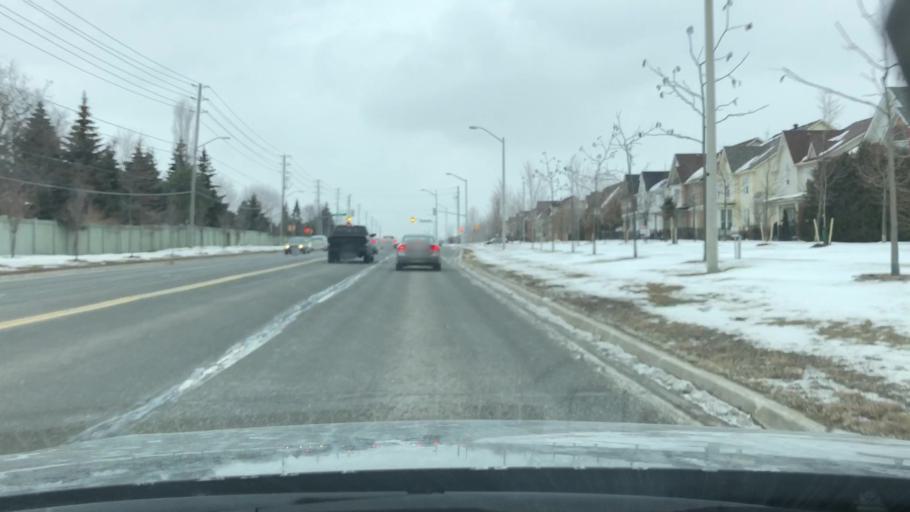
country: CA
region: Ontario
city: Markham
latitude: 43.8933
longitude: -79.2384
